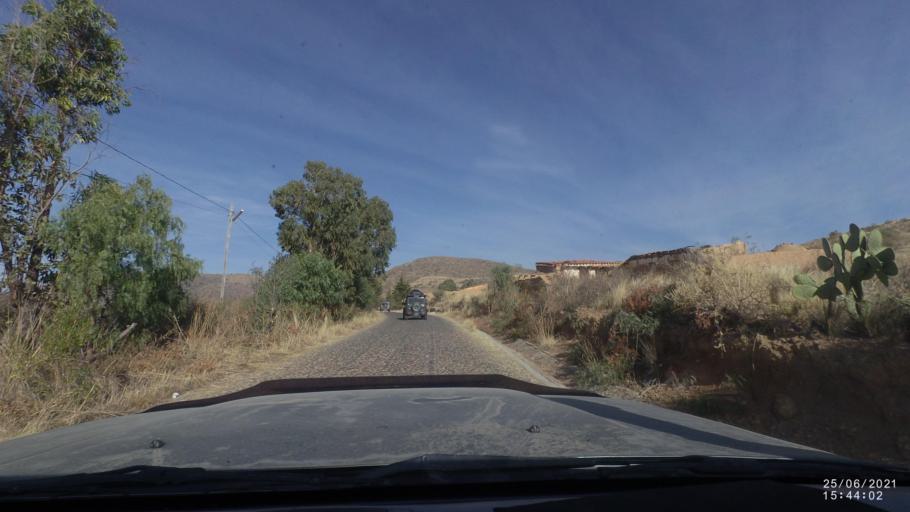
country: BO
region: Cochabamba
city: Cliza
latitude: -17.6538
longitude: -65.9127
